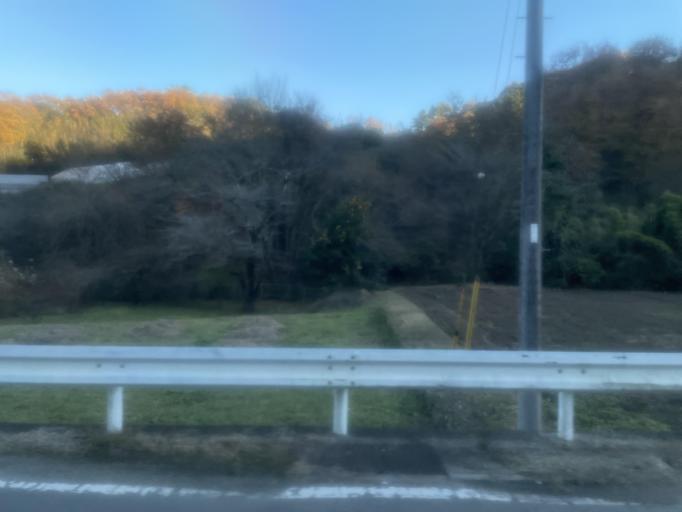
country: JP
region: Saitama
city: Yorii
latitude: 36.0948
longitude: 139.1751
